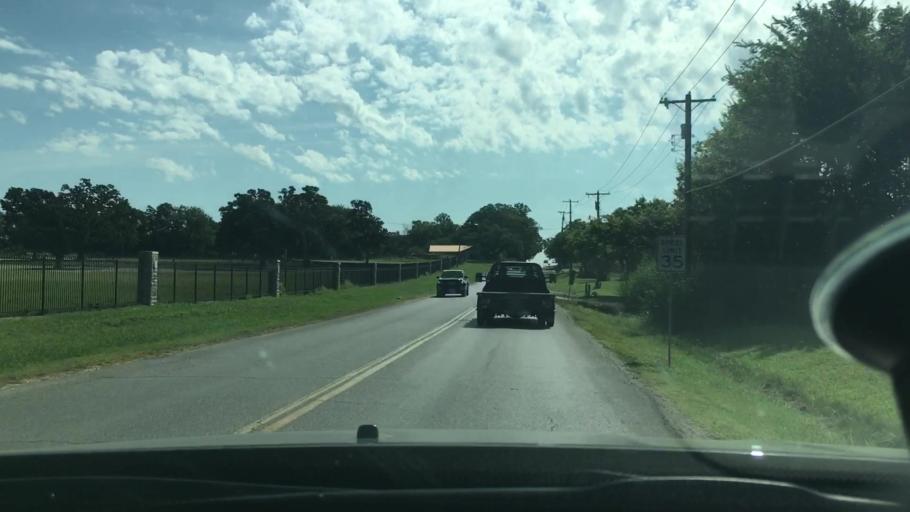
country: US
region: Oklahoma
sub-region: Carter County
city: Ardmore
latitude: 34.1585
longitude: -97.1206
